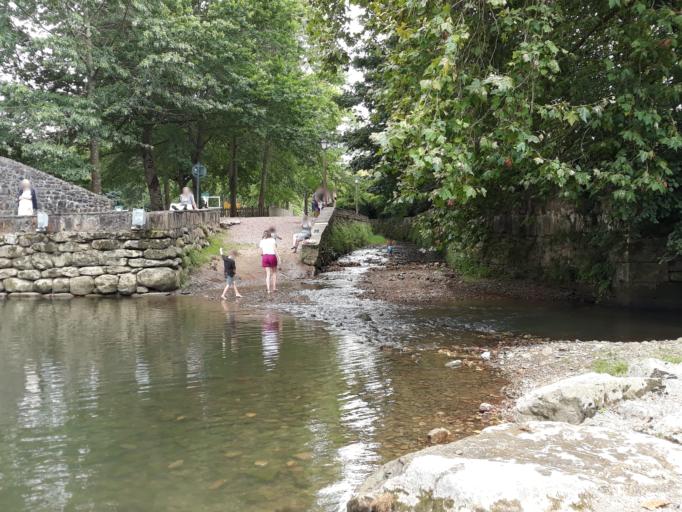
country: FR
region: Aquitaine
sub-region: Departement des Pyrenees-Atlantiques
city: Ascain
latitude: 43.3504
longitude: -1.6221
